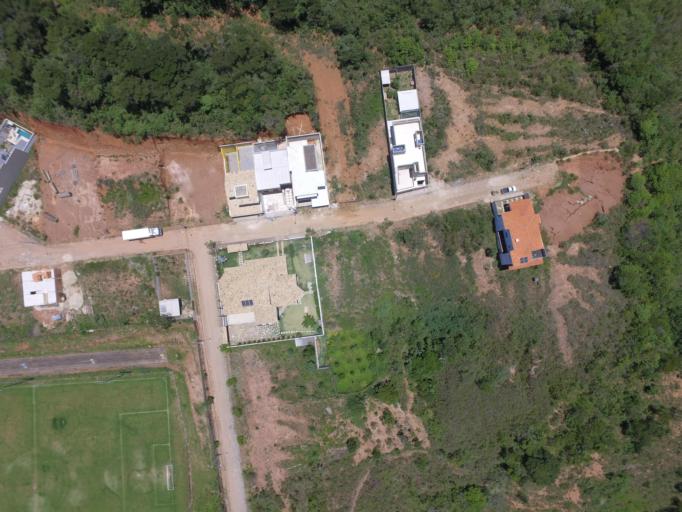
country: BR
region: Minas Gerais
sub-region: Tiradentes
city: Tiradentes
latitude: -21.0648
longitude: -44.0796
